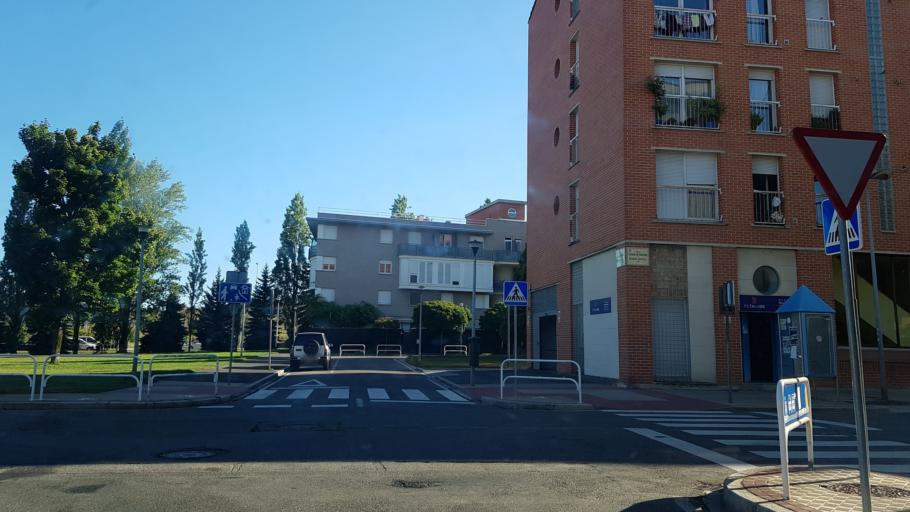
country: ES
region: Navarre
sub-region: Provincia de Navarra
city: Burlata
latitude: 42.8136
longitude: -1.6139
